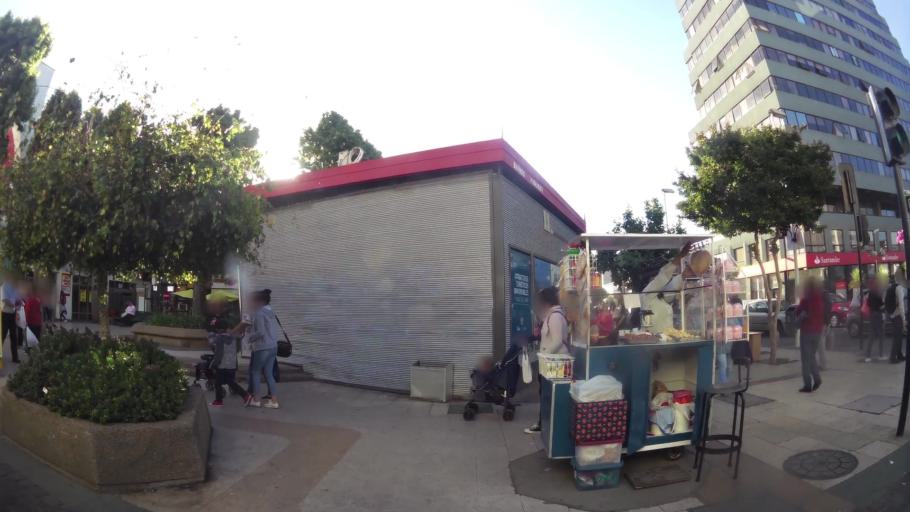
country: CL
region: Valparaiso
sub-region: Provincia de Valparaiso
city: Vina del Mar
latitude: -33.0244
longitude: -71.5571
